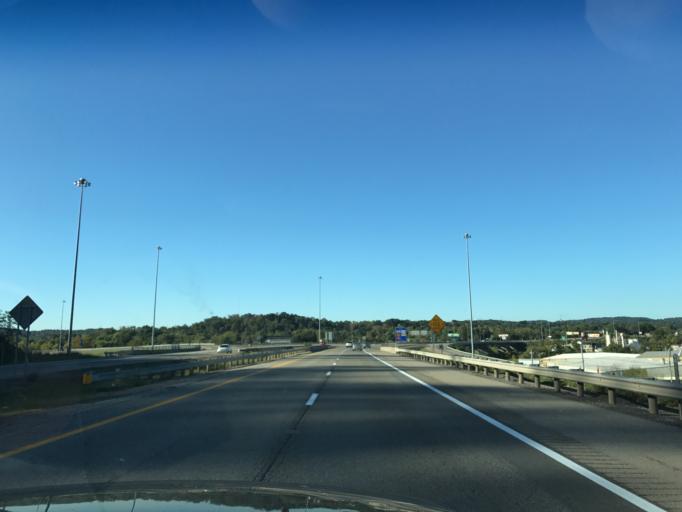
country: US
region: West Virginia
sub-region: Wood County
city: Parkersburg
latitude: 39.2590
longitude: -81.5304
